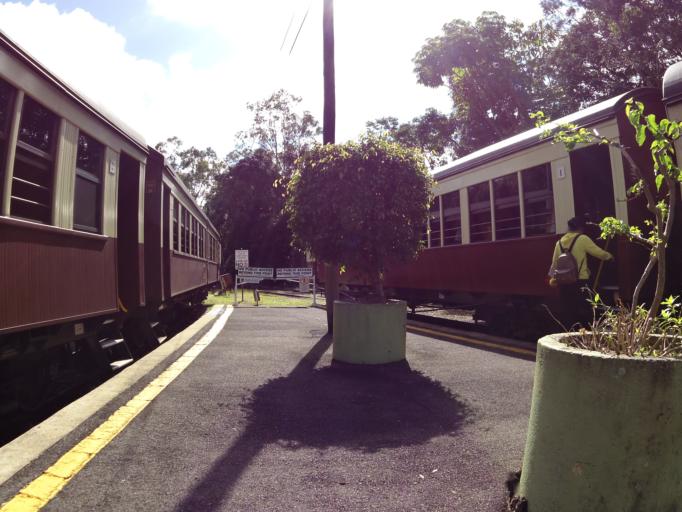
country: AU
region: Queensland
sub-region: Tablelands
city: Kuranda
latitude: -16.8178
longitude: 145.6382
